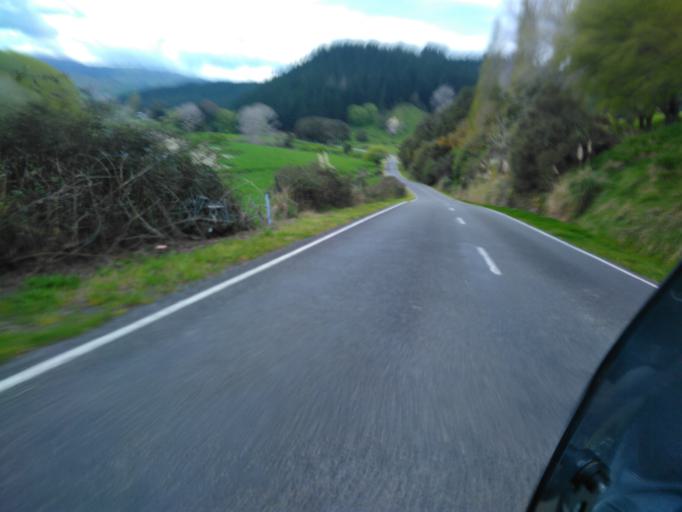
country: NZ
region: Hawke's Bay
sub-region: Wairoa District
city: Wairoa
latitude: -38.8999
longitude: 177.4708
